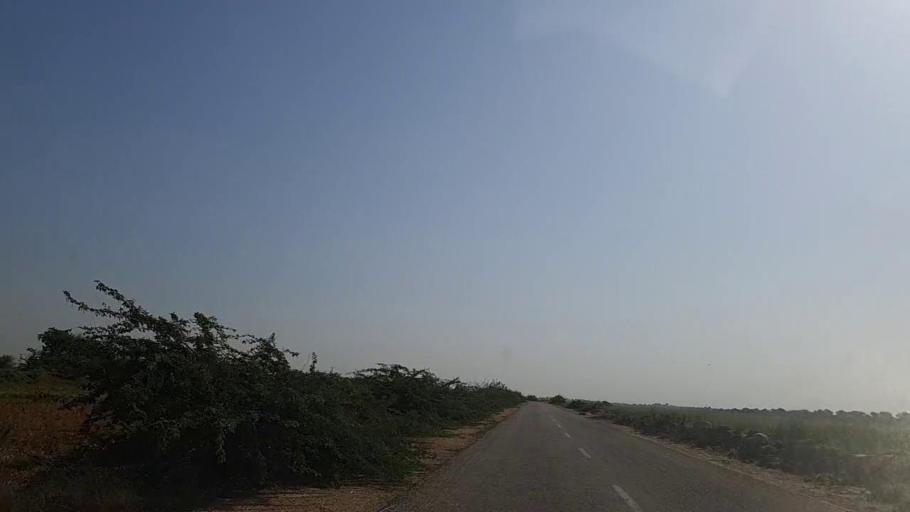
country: PK
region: Sindh
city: Jati
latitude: 24.5069
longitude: 68.2745
